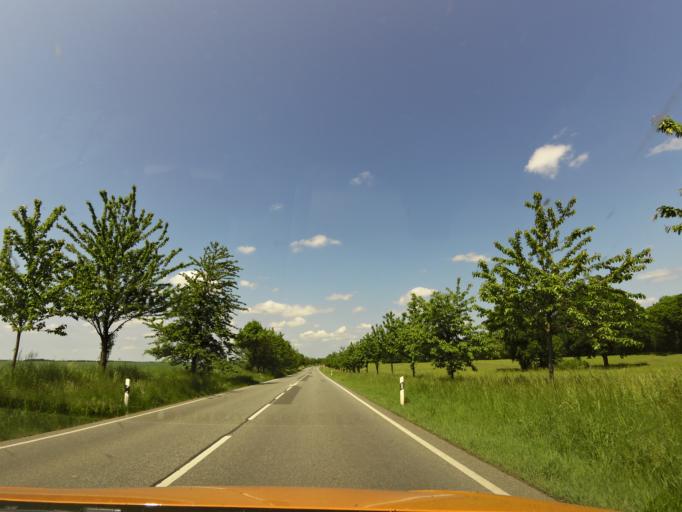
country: DE
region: Mecklenburg-Vorpommern
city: Lutzow
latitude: 53.6744
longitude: 11.1474
